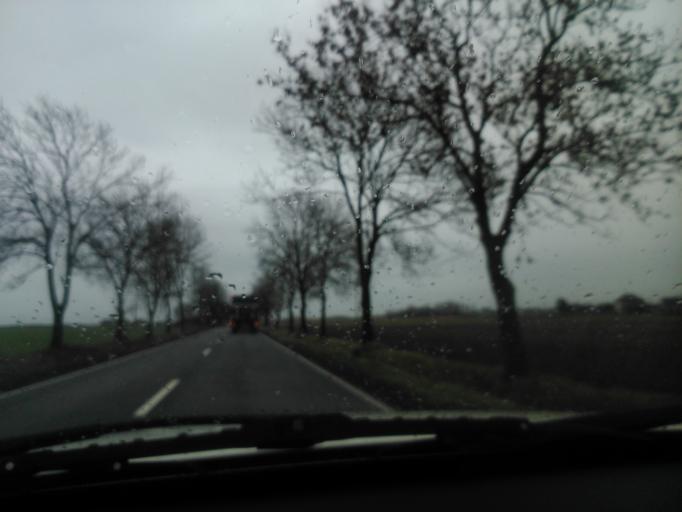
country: PL
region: Kujawsko-Pomorskie
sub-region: Powiat rypinski
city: Brzuze
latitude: 53.0702
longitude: 19.2560
